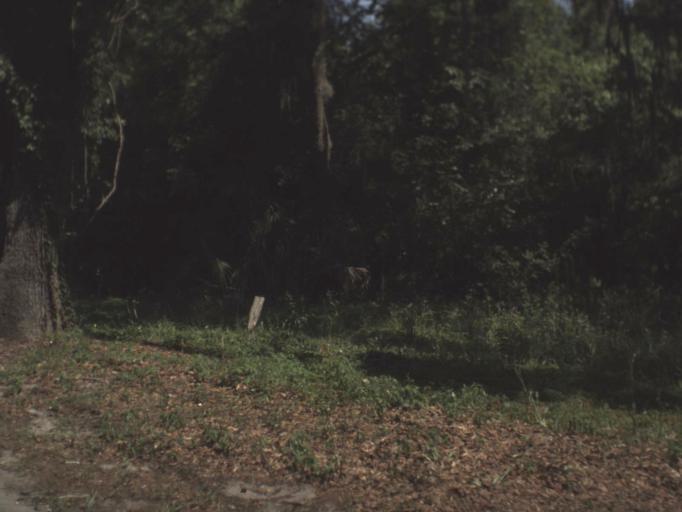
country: US
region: Florida
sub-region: Duval County
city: Jacksonville
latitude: 30.3653
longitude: -81.7404
